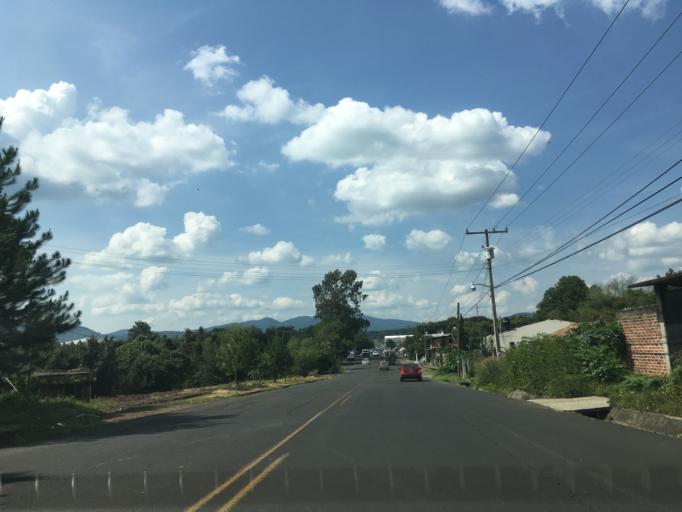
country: MX
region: Michoacan
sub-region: Tingueindin
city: Tingueindin
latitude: 19.7710
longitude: -102.4979
